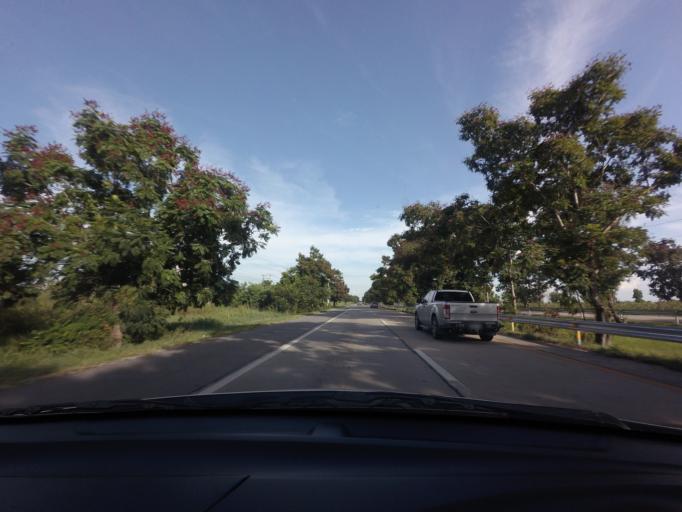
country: TH
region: Phra Nakhon Si Ayutthaya
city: Lat Bua Luang
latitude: 14.2266
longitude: 100.2768
